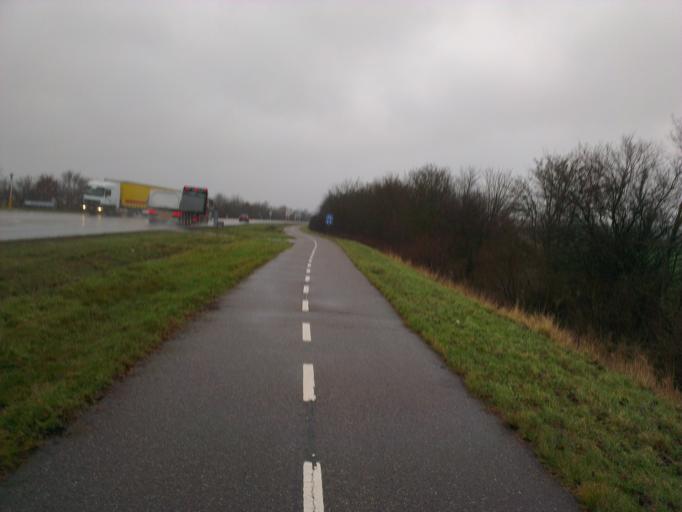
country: DK
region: Capital Region
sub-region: Frederikssund Kommune
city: Frederikssund
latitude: 55.8299
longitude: 12.0164
